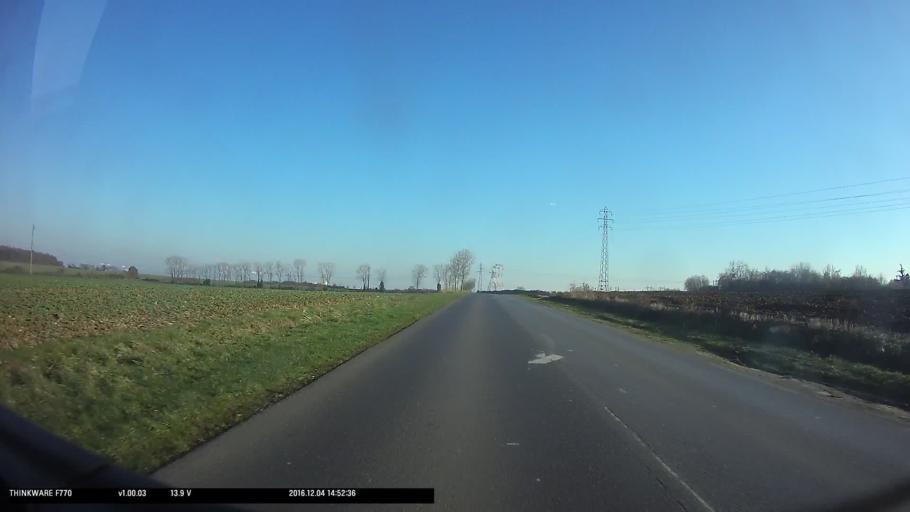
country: FR
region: Ile-de-France
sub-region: Departement du Val-d'Oise
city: Courdimanche
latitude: 49.0607
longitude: 2.0039
